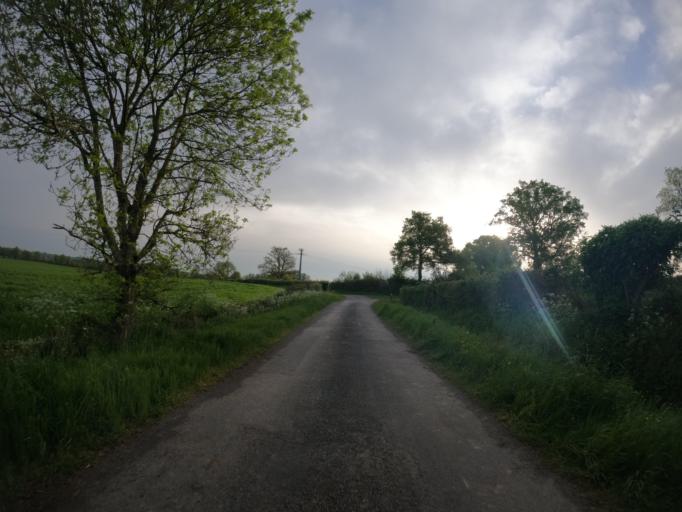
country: FR
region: Poitou-Charentes
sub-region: Departement des Deux-Sevres
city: Moncoutant
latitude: 46.7302
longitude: -0.5578
